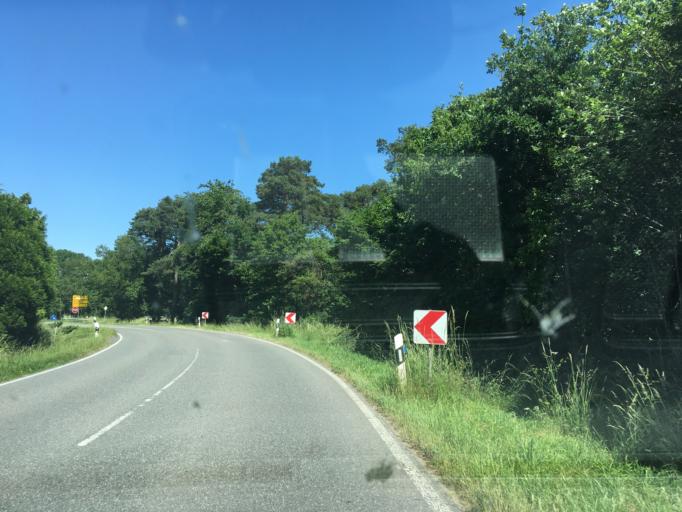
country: DE
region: North Rhine-Westphalia
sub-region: Regierungsbezirk Munster
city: Borken
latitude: 51.8157
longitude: 6.8147
